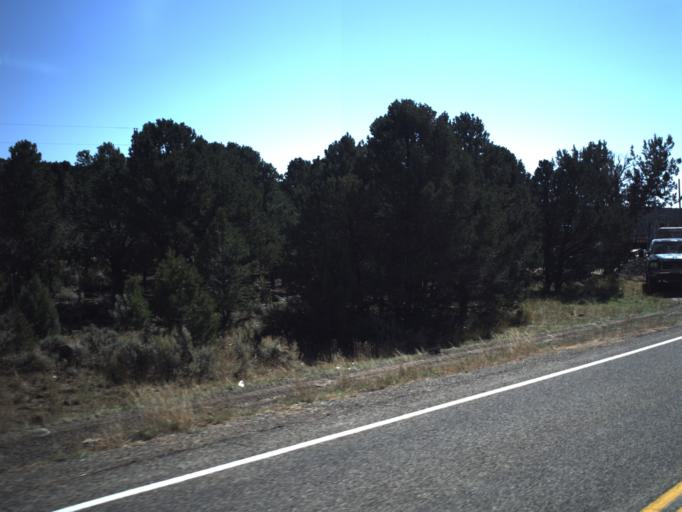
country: US
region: Utah
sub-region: Wayne County
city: Loa
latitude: 37.9564
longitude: -111.4356
